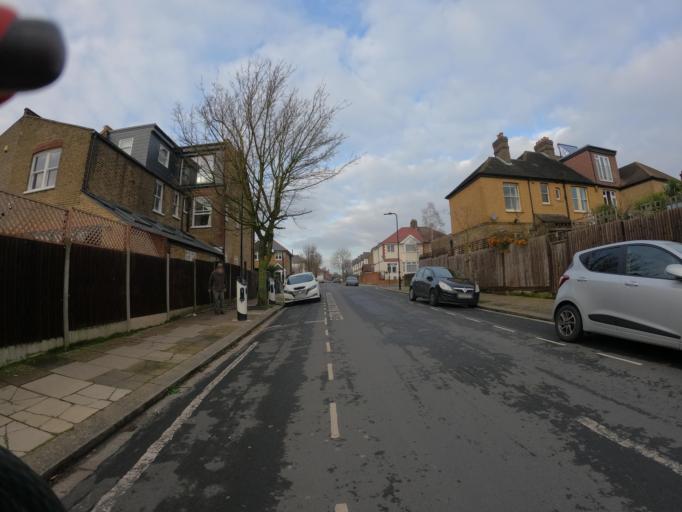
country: GB
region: England
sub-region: Greater London
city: Greenford
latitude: 51.5145
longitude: -0.3309
